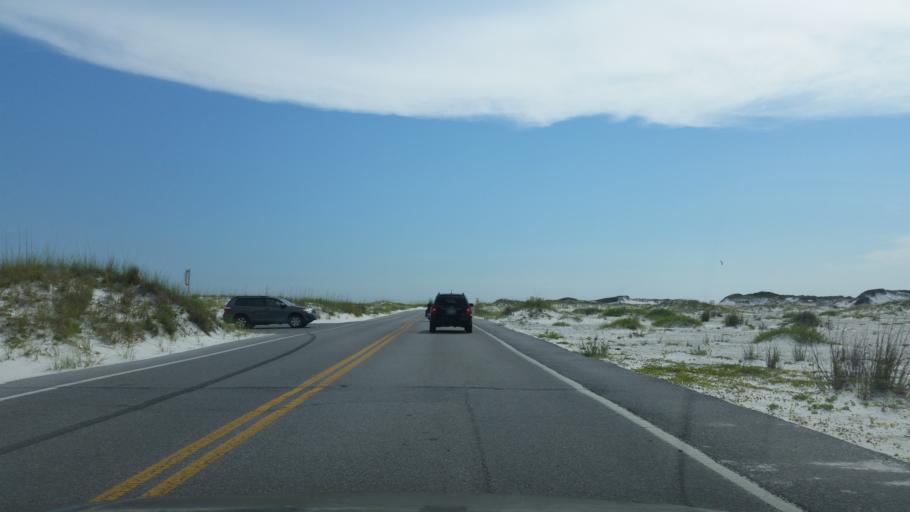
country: US
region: Florida
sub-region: Santa Rosa County
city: Woodlawn Beach
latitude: 30.3595
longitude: -86.9929
